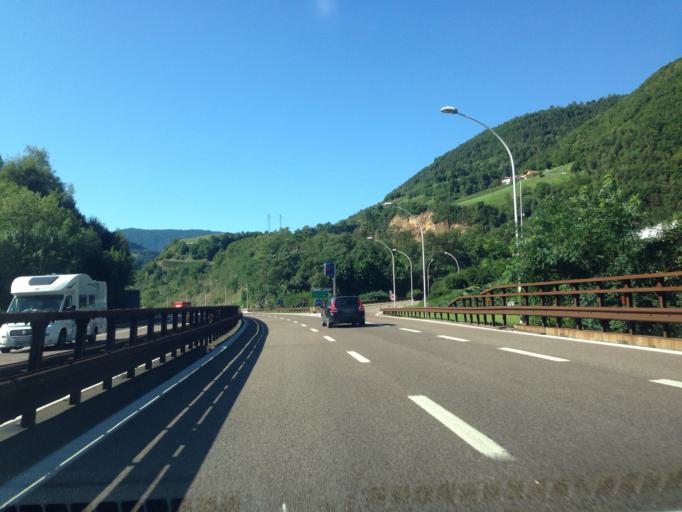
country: IT
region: Trentino-Alto Adige
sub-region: Bolzano
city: Fie Allo Sciliar
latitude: 46.5316
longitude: 11.4917
